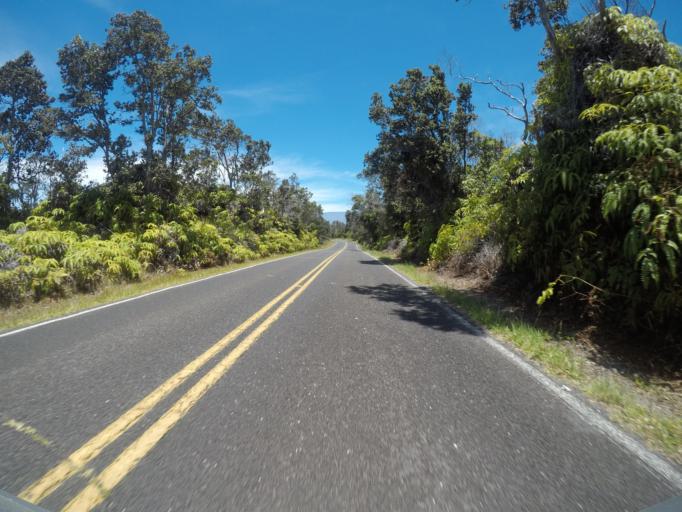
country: US
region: Hawaii
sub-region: Hawaii County
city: Volcano
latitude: 19.3661
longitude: -155.2195
